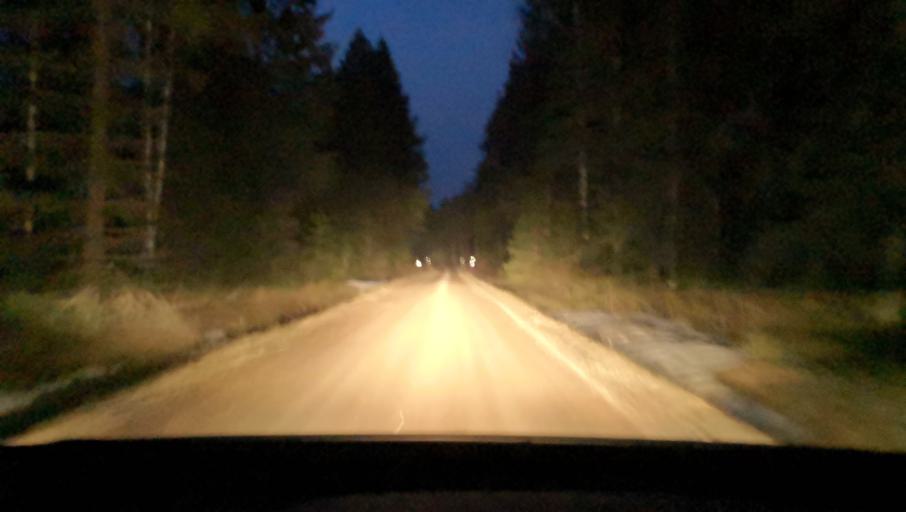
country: SE
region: OErebro
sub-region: Lindesbergs Kommun
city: Frovi
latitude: 59.6578
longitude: 15.4972
